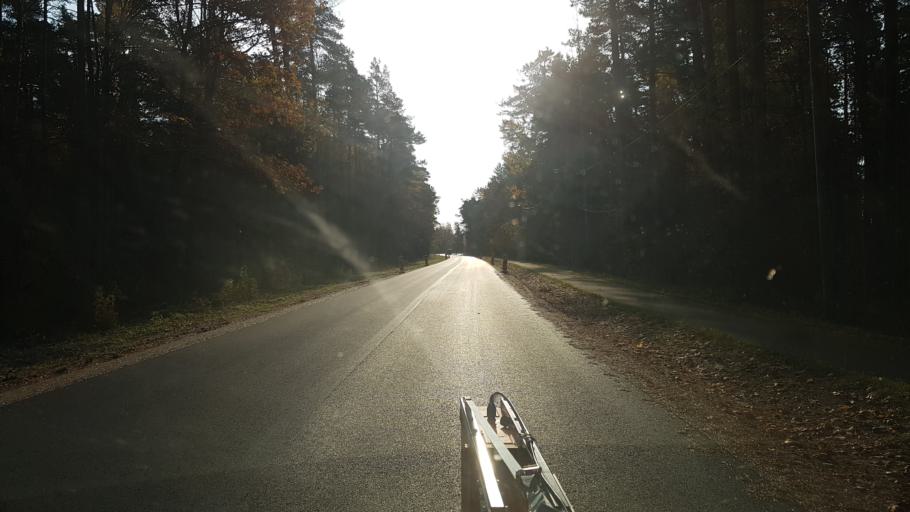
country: EE
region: Paernumaa
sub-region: Paikuse vald
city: Paikuse
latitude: 58.3663
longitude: 24.6016
